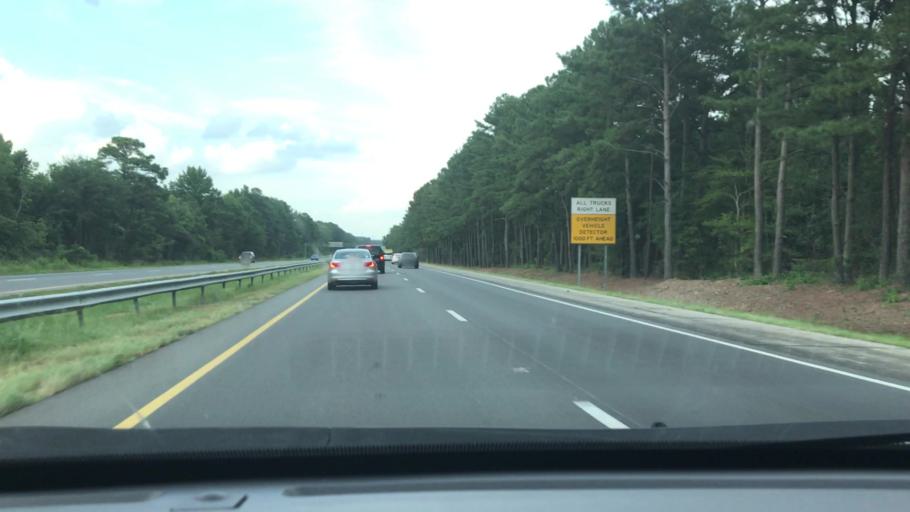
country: US
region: North Carolina
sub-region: Harnett County
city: Erwin
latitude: 35.1869
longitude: -78.6867
